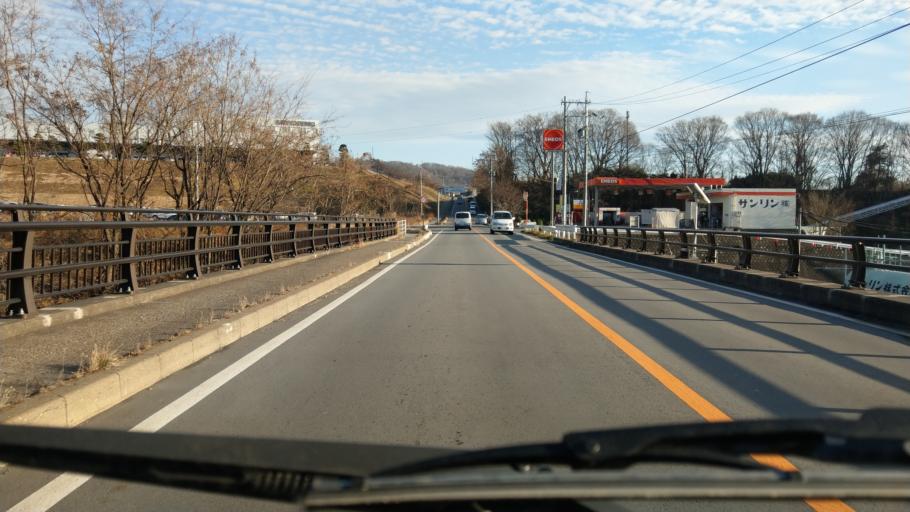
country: JP
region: Nagano
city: Ueda
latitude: 36.3985
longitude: 138.2938
